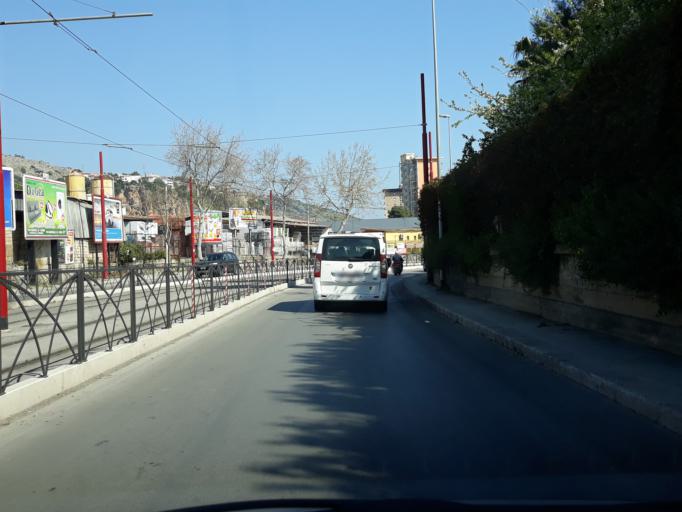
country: IT
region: Sicily
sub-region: Palermo
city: Palermo
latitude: 38.1298
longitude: 13.3031
